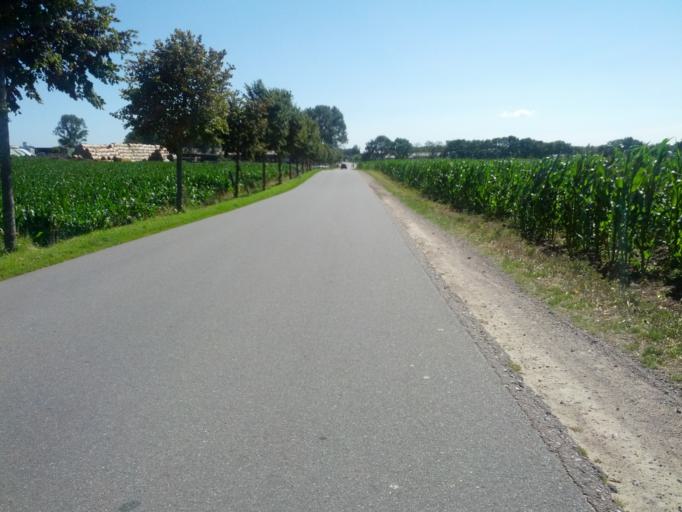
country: DE
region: Mecklenburg-Vorpommern
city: Bastorf
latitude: 54.1279
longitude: 11.6859
